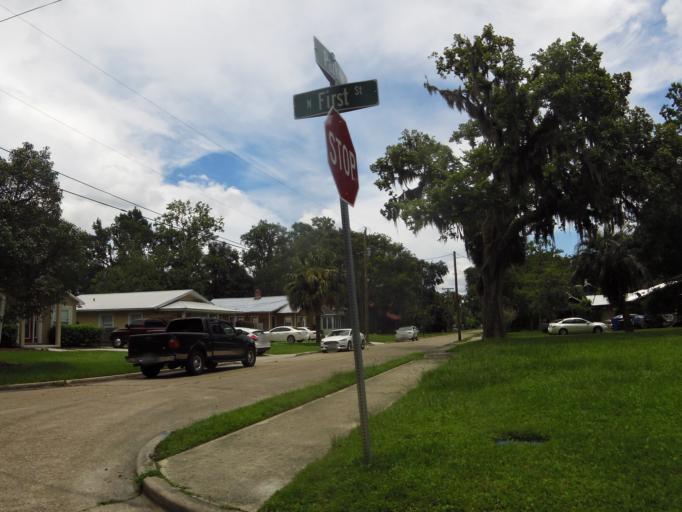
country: US
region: Florida
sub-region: Putnam County
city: East Palatka
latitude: 29.7191
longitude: -81.5069
